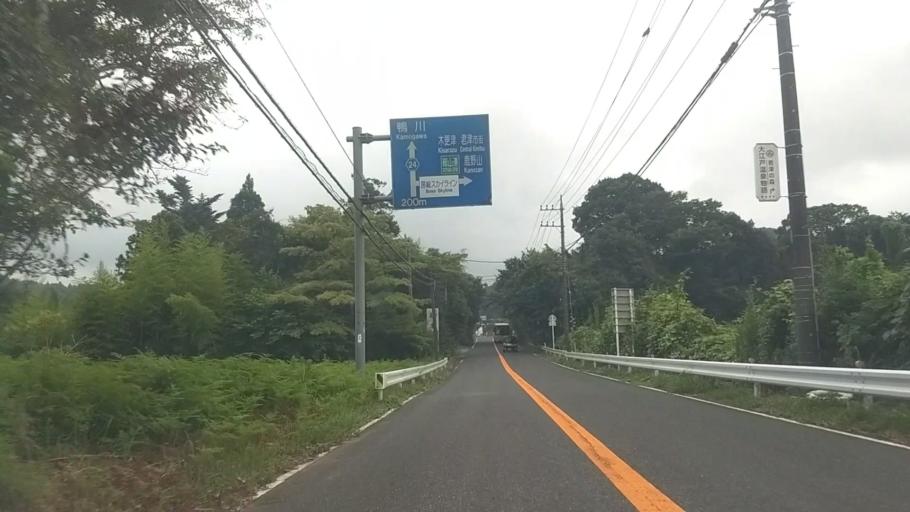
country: JP
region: Chiba
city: Kawaguchi
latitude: 35.2073
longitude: 140.0707
